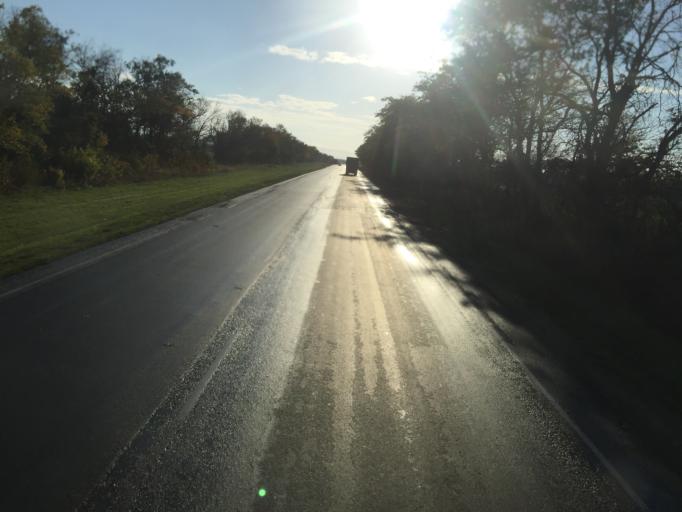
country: RU
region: Rostov
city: Zernograd
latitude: 46.7972
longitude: 40.3728
